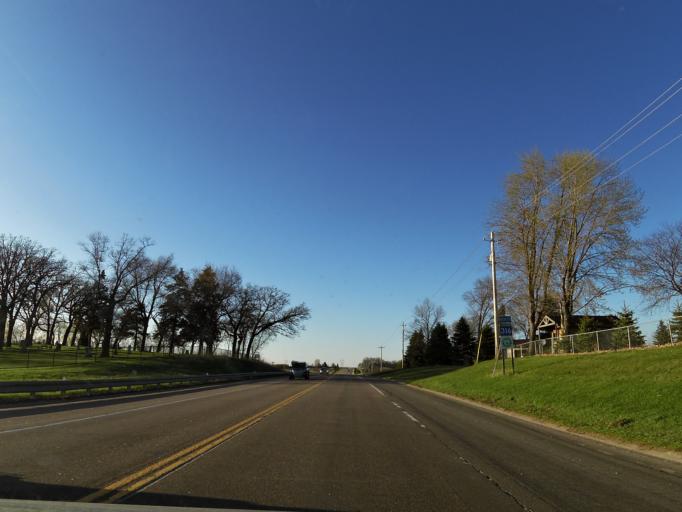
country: US
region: Wisconsin
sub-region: Pierce County
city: Prescott
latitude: 44.6152
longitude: -92.7723
